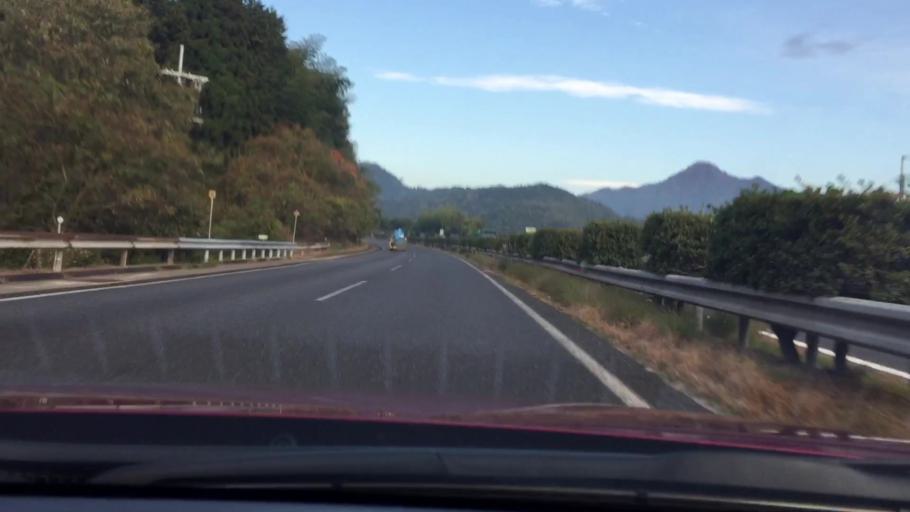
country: JP
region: Hyogo
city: Yamazakicho-nakabirose
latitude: 34.9661
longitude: 134.6772
